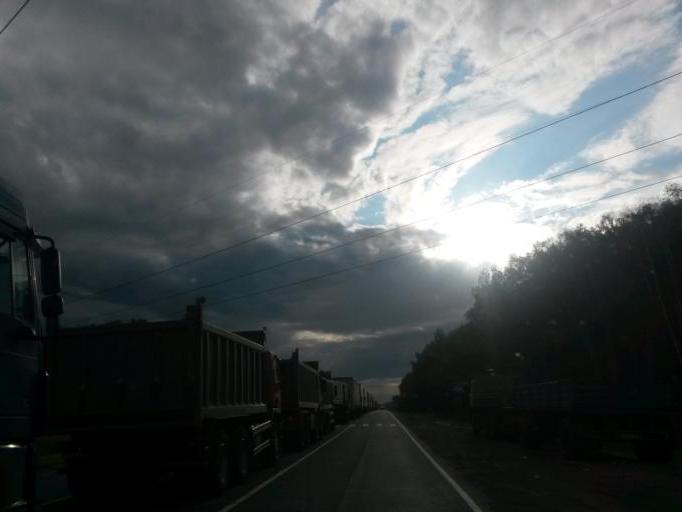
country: RU
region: Moskovskaya
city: L'vovskiy
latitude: 55.3324
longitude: 37.5447
